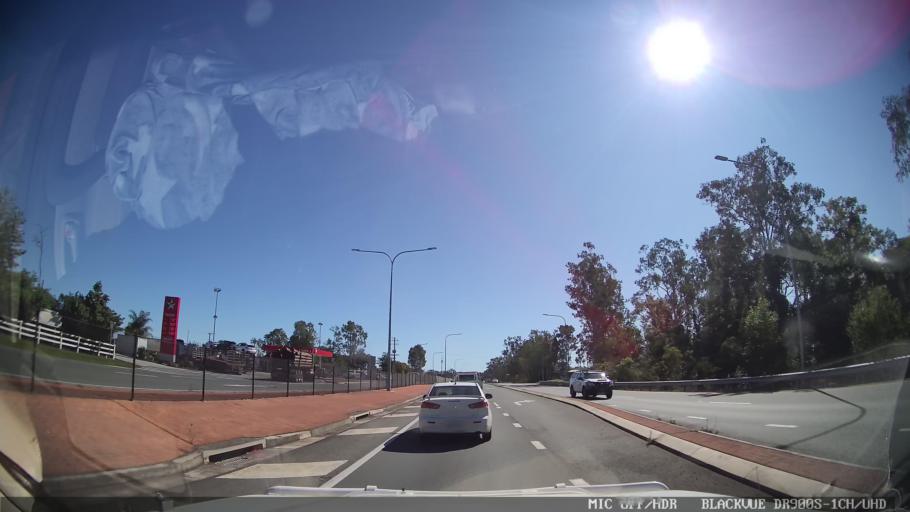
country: AU
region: Queensland
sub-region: Gympie Regional Council
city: Monkland
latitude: -26.2391
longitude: 152.6997
